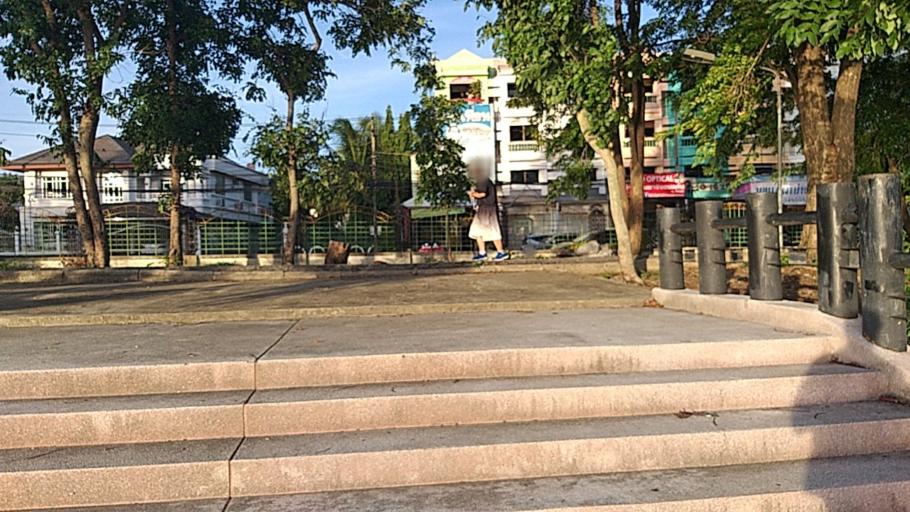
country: TH
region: Khon Kaen
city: Khon Kaen
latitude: 16.4169
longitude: 102.8407
